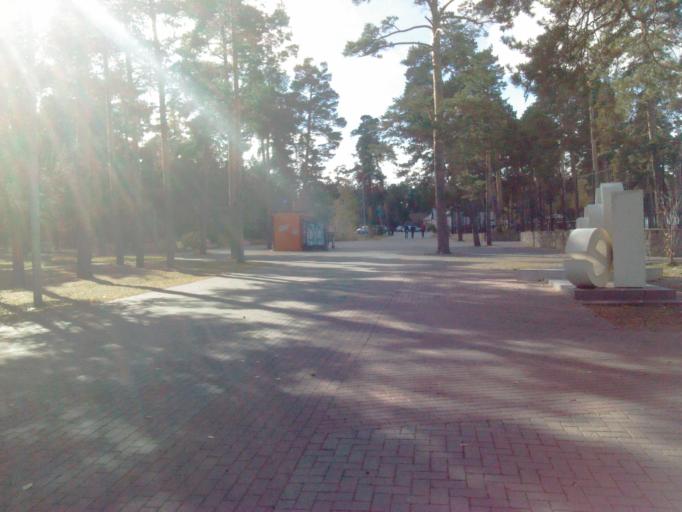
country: RU
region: Chelyabinsk
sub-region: Gorod Chelyabinsk
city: Chelyabinsk
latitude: 55.1641
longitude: 61.3657
